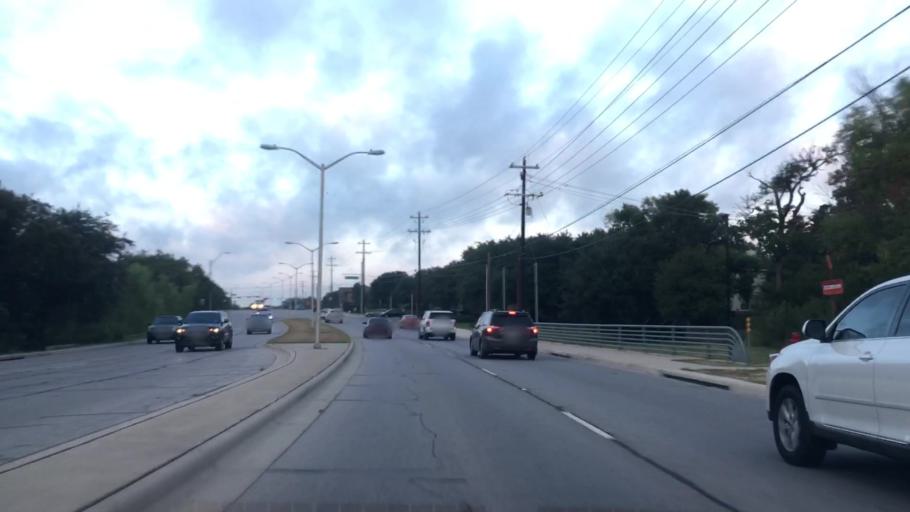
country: US
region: Texas
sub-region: Williamson County
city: Cedar Park
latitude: 30.5057
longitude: -97.7989
